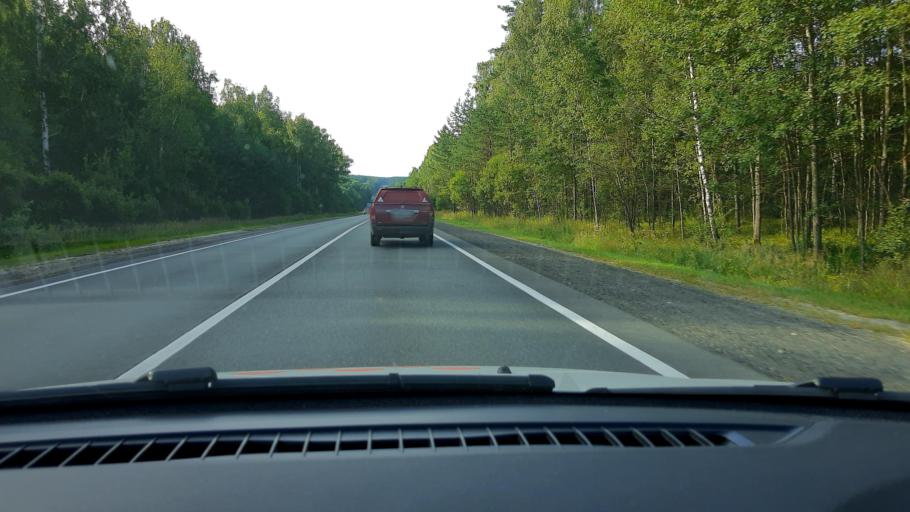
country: RU
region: Nizjnij Novgorod
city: Dal'neye Konstantinovo
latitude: 55.9234
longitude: 43.9827
